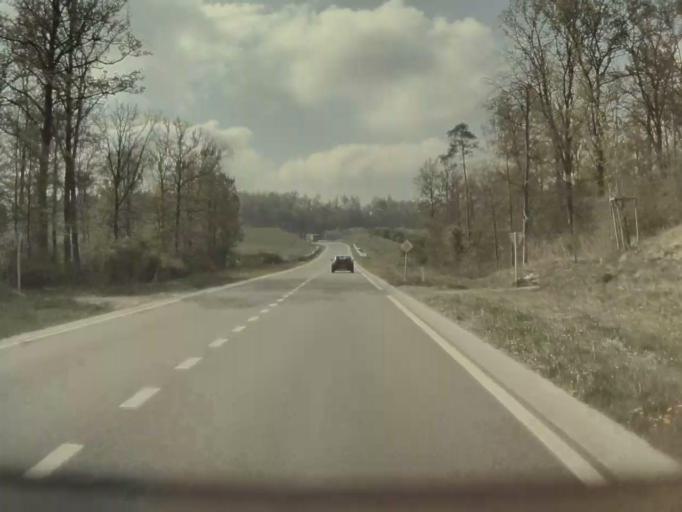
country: BE
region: Wallonia
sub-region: Province du Luxembourg
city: Marche-en-Famenne
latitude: 50.2208
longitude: 5.3150
